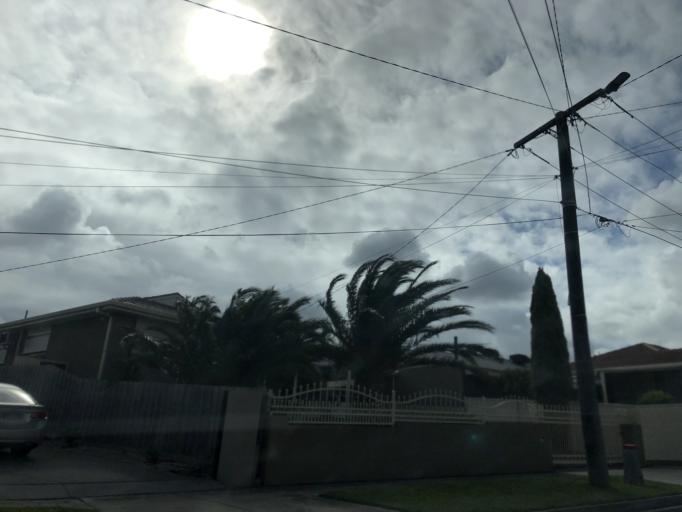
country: AU
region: Victoria
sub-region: Kingston
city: Clayton South
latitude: -37.9347
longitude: 145.1041
